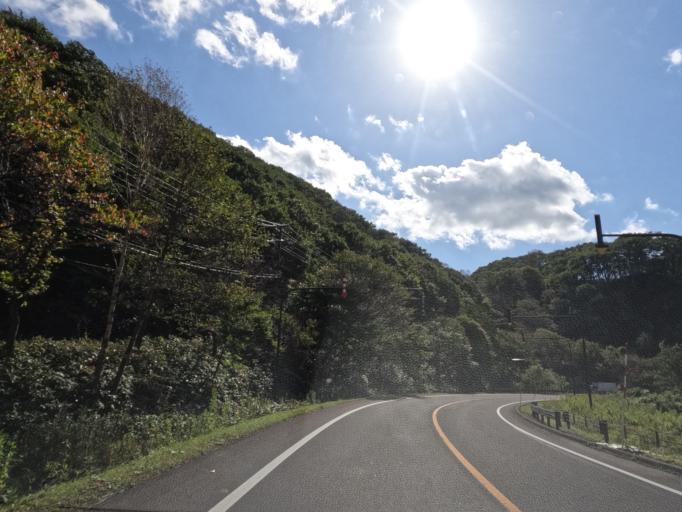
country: JP
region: Hokkaido
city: Shiraoi
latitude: 42.4833
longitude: 141.1459
